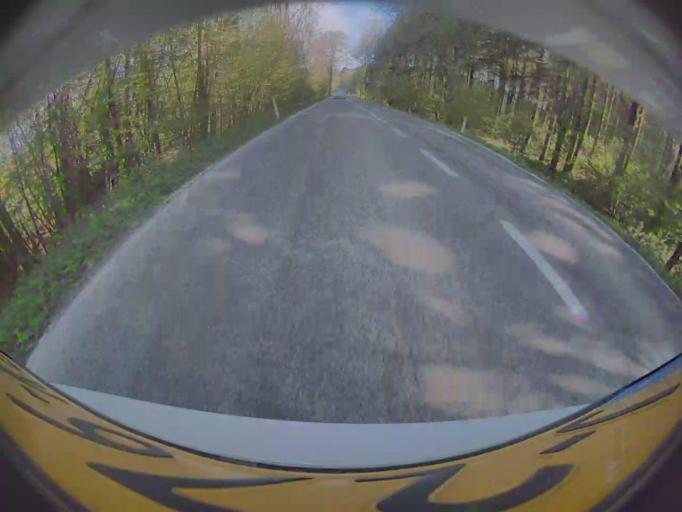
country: BE
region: Wallonia
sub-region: Province du Luxembourg
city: Tellin
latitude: 50.0292
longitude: 5.2066
